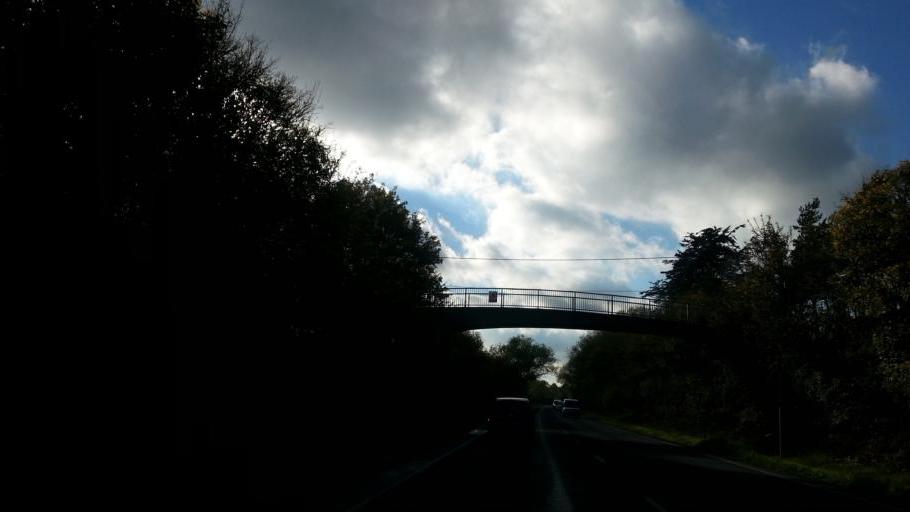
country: GB
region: England
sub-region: Suffolk
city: Bungay
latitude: 52.4582
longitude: 1.4300
